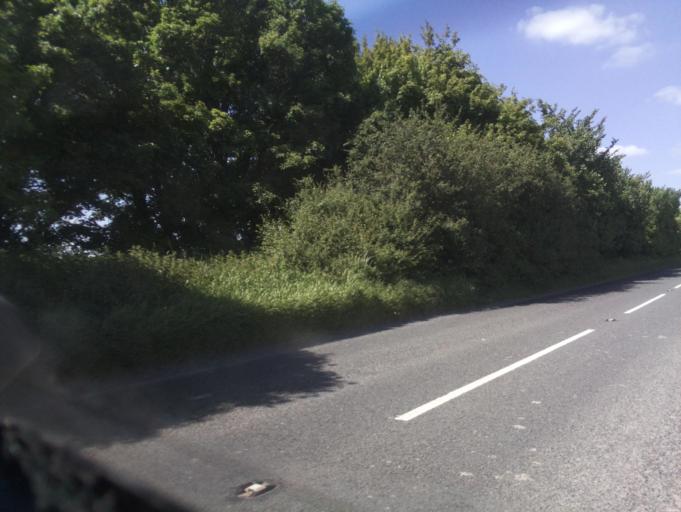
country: GB
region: England
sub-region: Wiltshire
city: Avebury
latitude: 51.4666
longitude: -1.8492
